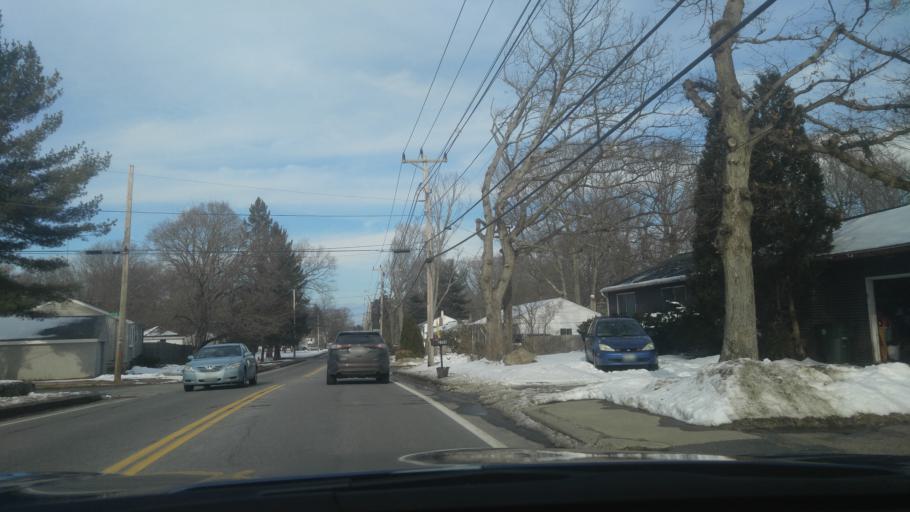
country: US
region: Rhode Island
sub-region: Kent County
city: West Warwick
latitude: 41.6688
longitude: -71.5361
